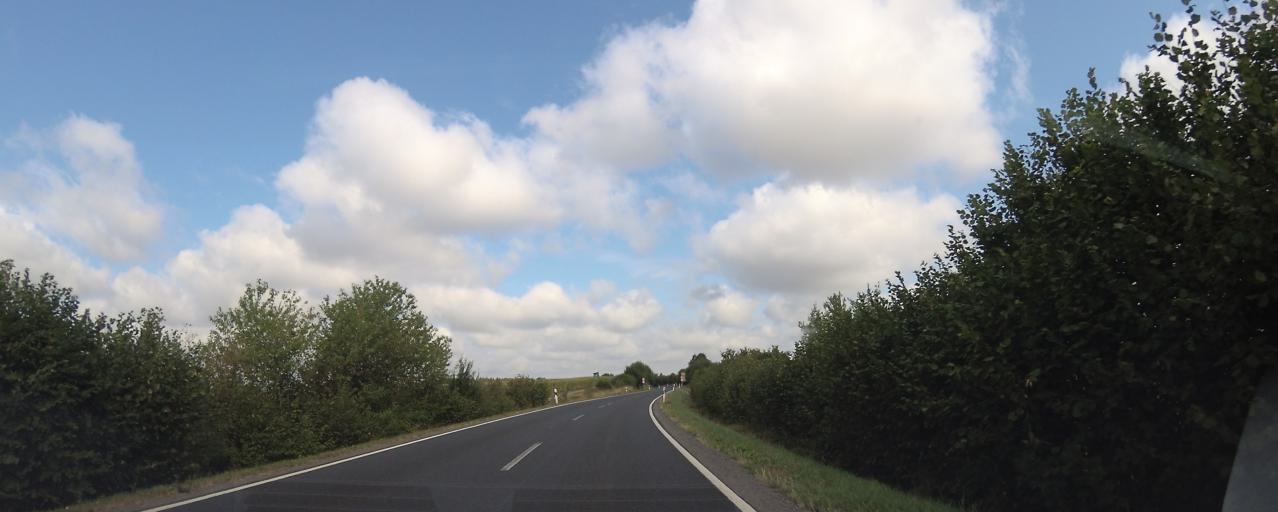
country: DE
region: Rheinland-Pfalz
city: Herforst
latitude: 49.9519
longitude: 6.6855
